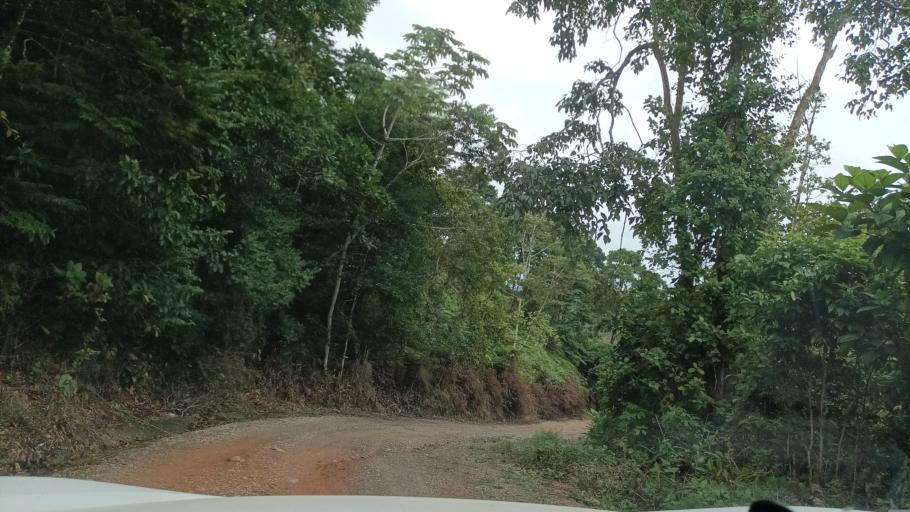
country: MX
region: Veracruz
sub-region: Uxpanapa
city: Poblado 10
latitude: 17.4308
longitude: -94.4205
